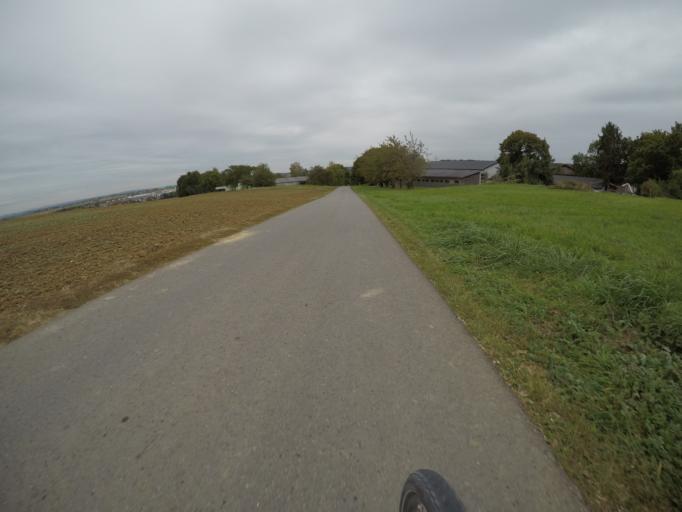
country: DE
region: Baden-Wuerttemberg
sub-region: Regierungsbezirk Stuttgart
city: Leonberg
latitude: 48.8384
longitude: 8.9887
